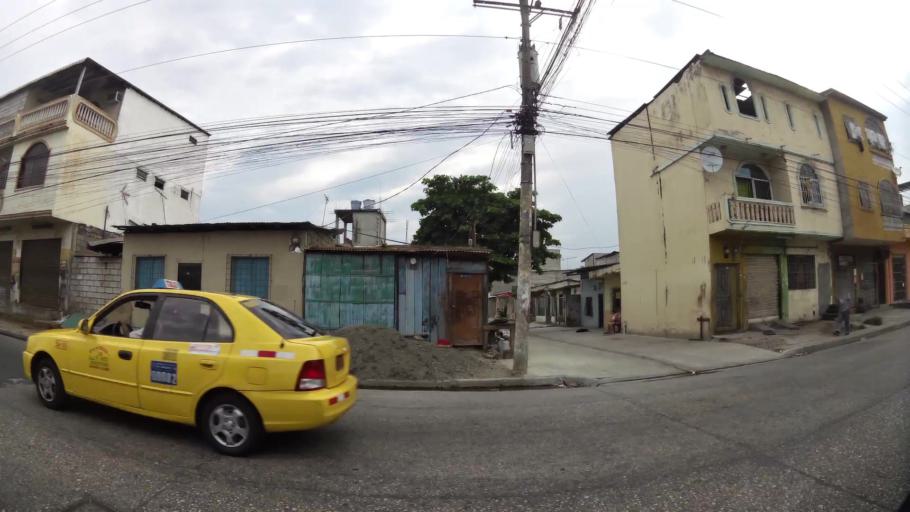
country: EC
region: Guayas
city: Guayaquil
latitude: -2.2491
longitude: -79.8797
